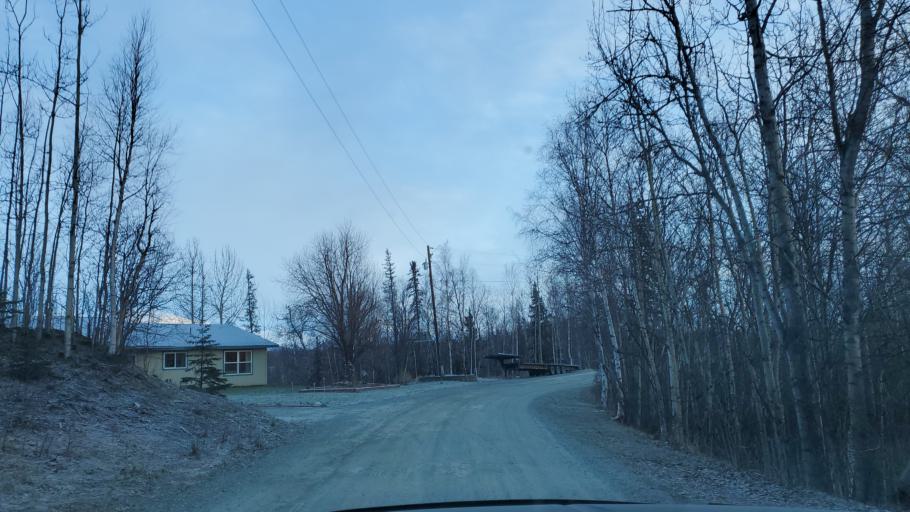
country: US
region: Alaska
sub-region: Matanuska-Susitna Borough
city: Lakes
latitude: 61.6018
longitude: -149.3144
